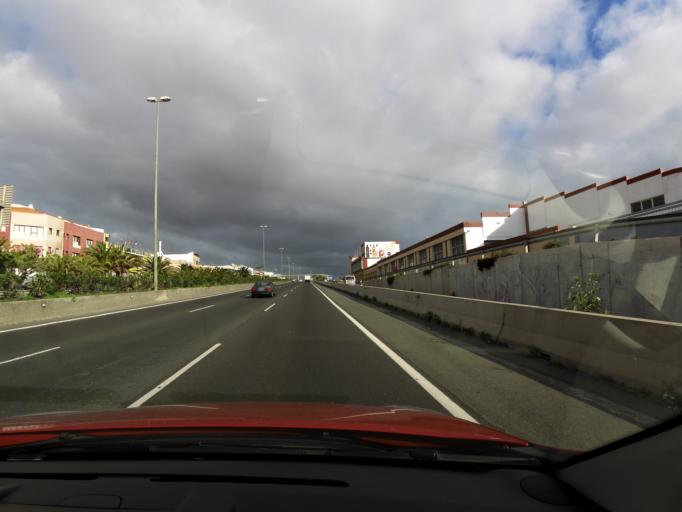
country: ES
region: Canary Islands
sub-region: Provincia de Las Palmas
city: Telde
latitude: 27.9823
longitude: -15.3916
